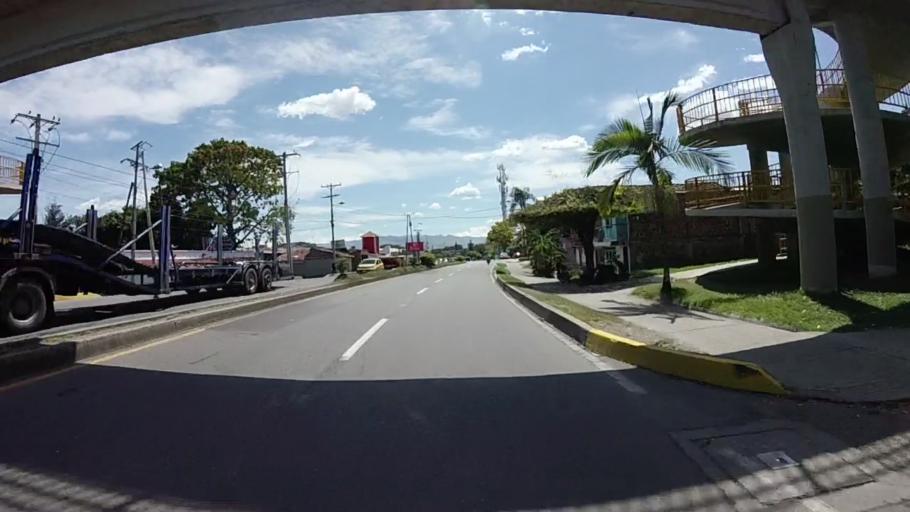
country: CO
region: Valle del Cauca
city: Cartago
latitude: 4.7321
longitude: -75.9085
